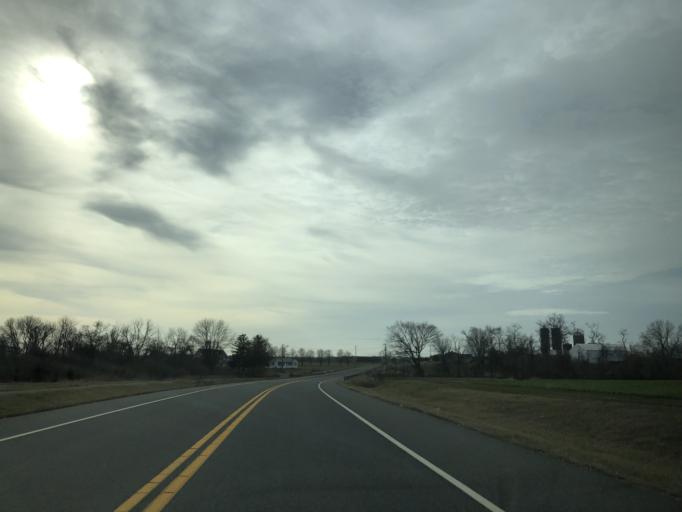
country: US
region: Delaware
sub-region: New Castle County
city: Middletown
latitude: 39.5159
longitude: -75.6787
